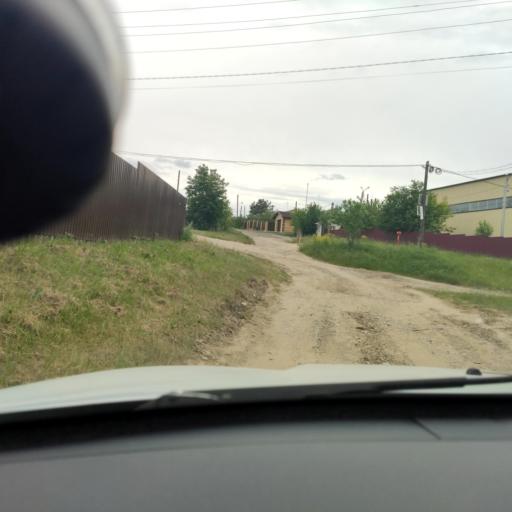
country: RU
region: Perm
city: Polazna
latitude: 58.3016
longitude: 56.4021
